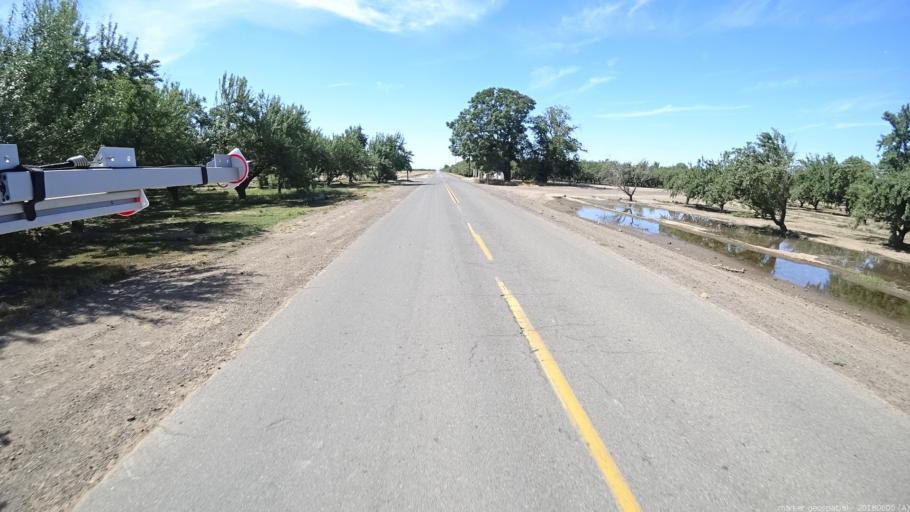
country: US
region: California
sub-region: Madera County
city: Chowchilla
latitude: 37.0477
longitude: -120.3831
